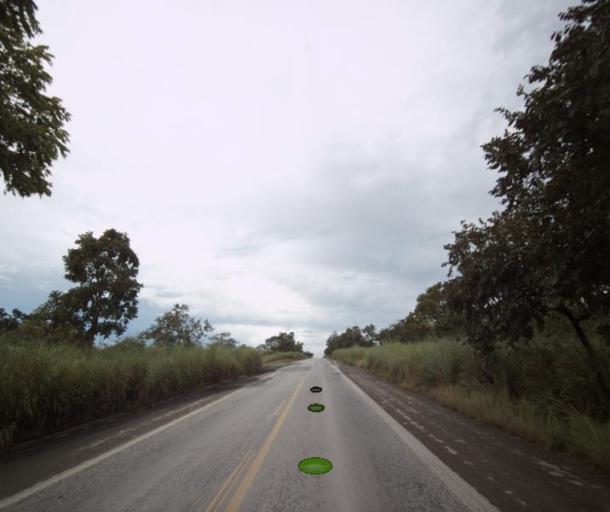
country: BR
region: Goias
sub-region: Porangatu
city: Porangatu
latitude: -13.5047
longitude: -49.1270
